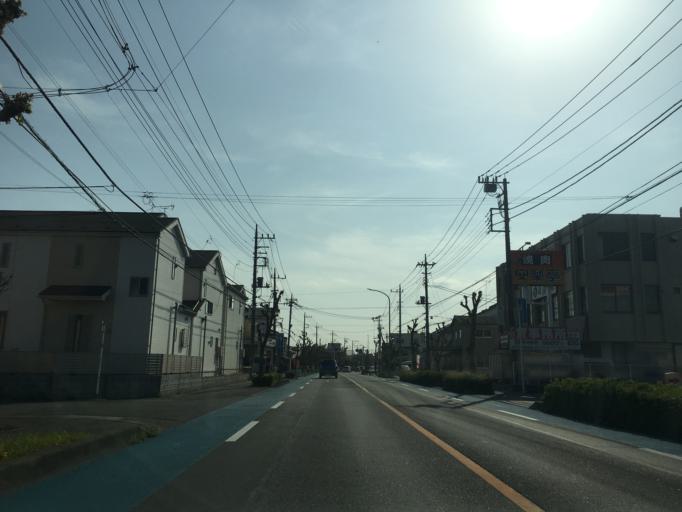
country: JP
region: Saitama
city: Ageoshimo
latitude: 35.9595
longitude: 139.5845
